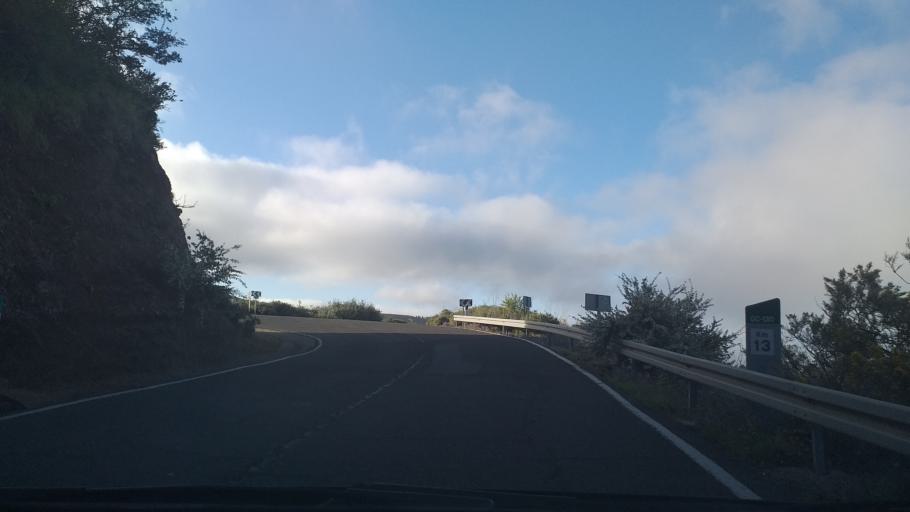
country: ES
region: Canary Islands
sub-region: Provincia de Las Palmas
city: Valsequillo de Gran Canaria
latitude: 27.9583
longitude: -15.5058
